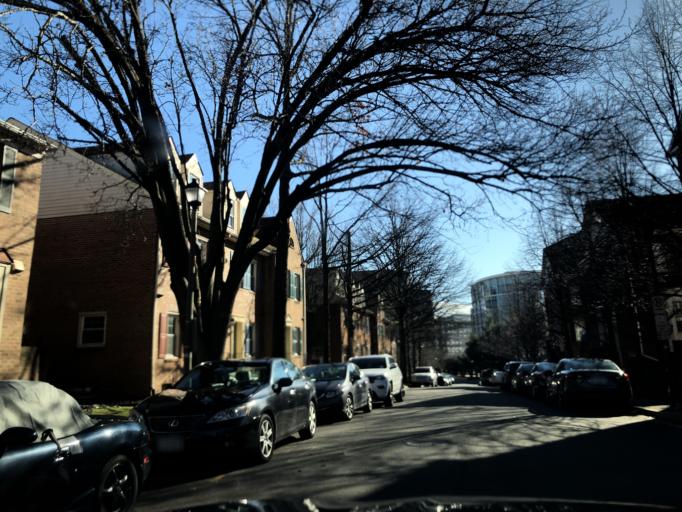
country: US
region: Virginia
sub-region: Arlington County
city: Arlington
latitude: 38.8849
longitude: -77.1161
